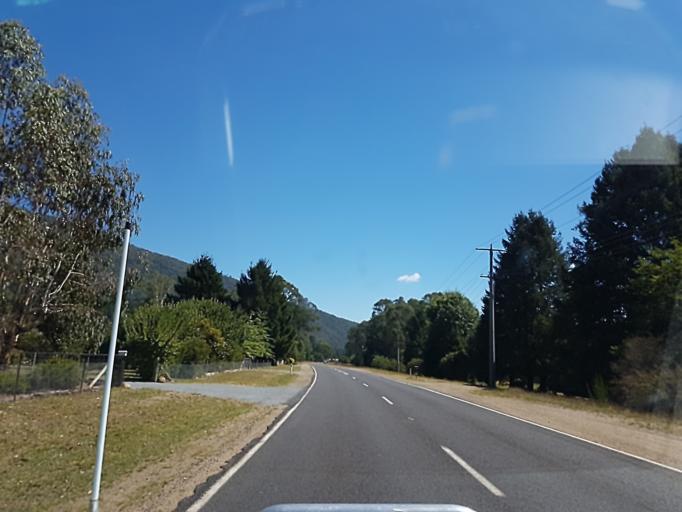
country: AU
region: Victoria
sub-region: Alpine
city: Mount Beauty
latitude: -36.7706
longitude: 147.0282
